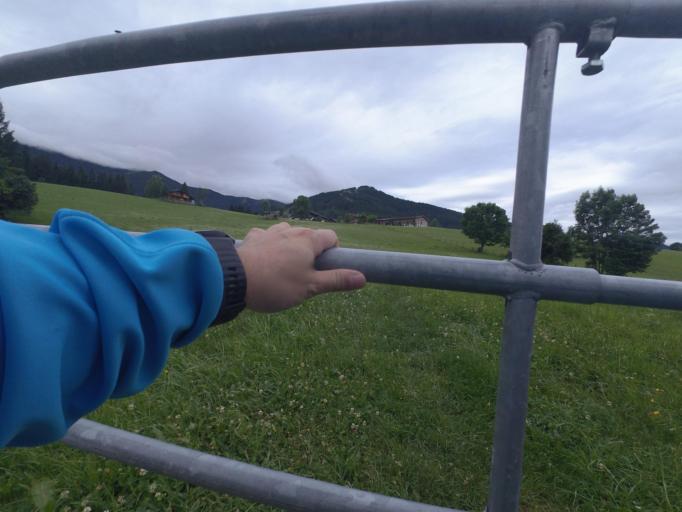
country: AT
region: Salzburg
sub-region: Politischer Bezirk Zell am See
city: Leogang
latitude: 47.4341
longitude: 12.7518
